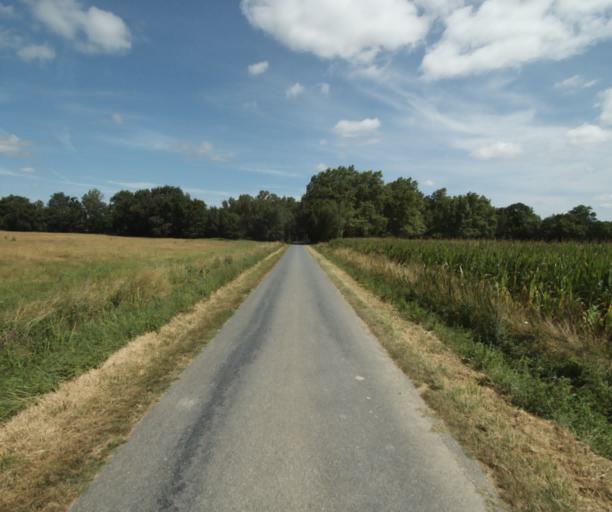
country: FR
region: Midi-Pyrenees
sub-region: Departement du Tarn
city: Soreze
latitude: 43.4914
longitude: 2.0797
